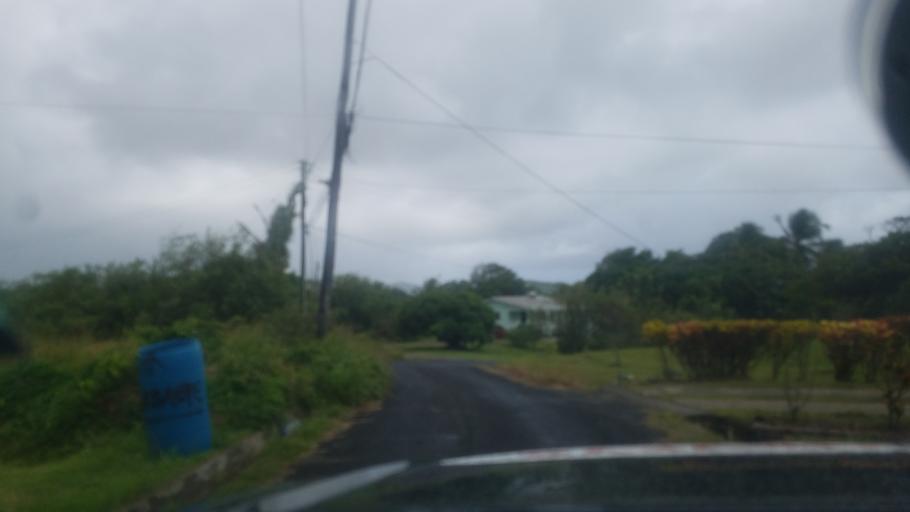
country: LC
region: Laborie Quarter
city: Laborie
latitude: 13.7667
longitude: -60.9723
